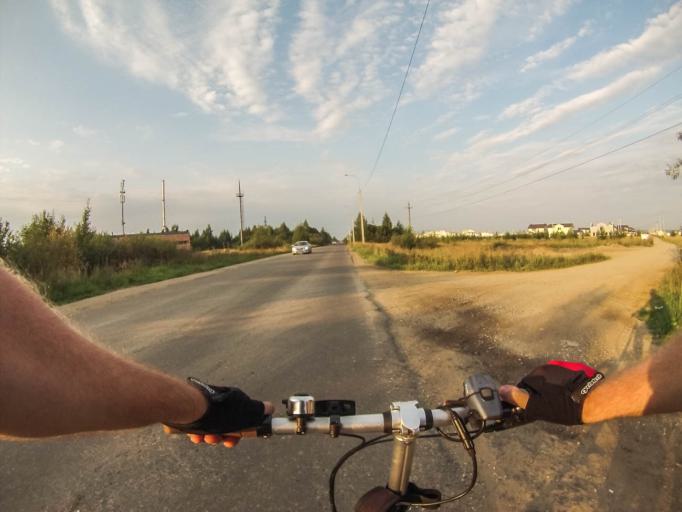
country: RU
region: Kostroma
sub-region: Kostromskoy Rayon
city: Kostroma
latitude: 57.8267
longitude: 40.8893
